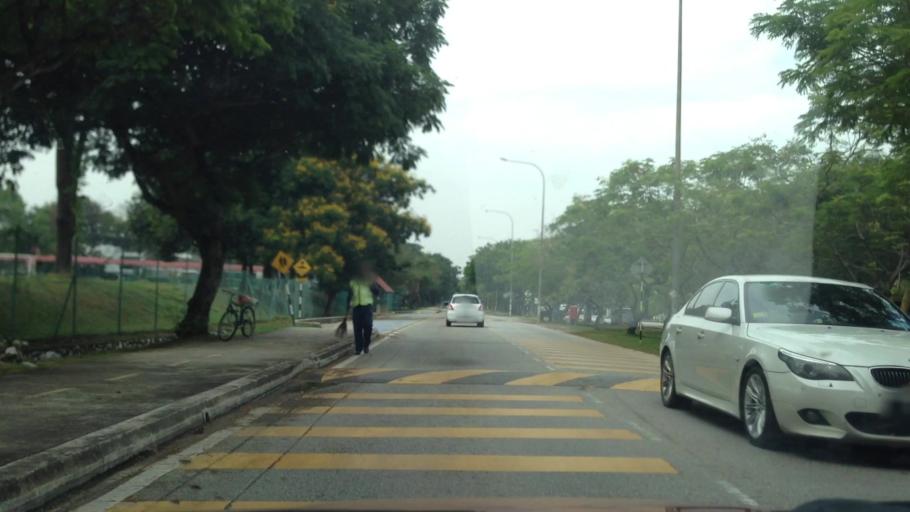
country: MY
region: Selangor
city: Subang Jaya
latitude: 3.0559
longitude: 101.5739
